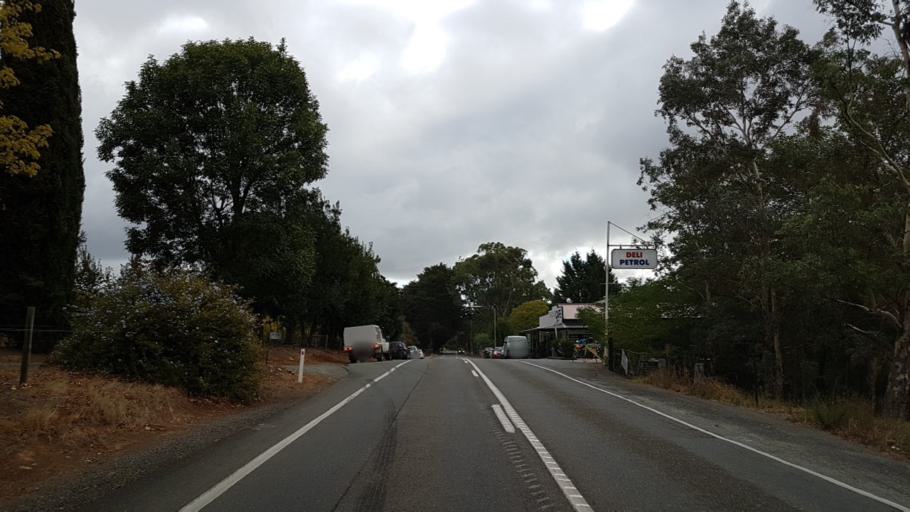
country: AU
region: South Australia
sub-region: Adelaide Hills
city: Gumeracha
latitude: -34.8404
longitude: 138.8296
